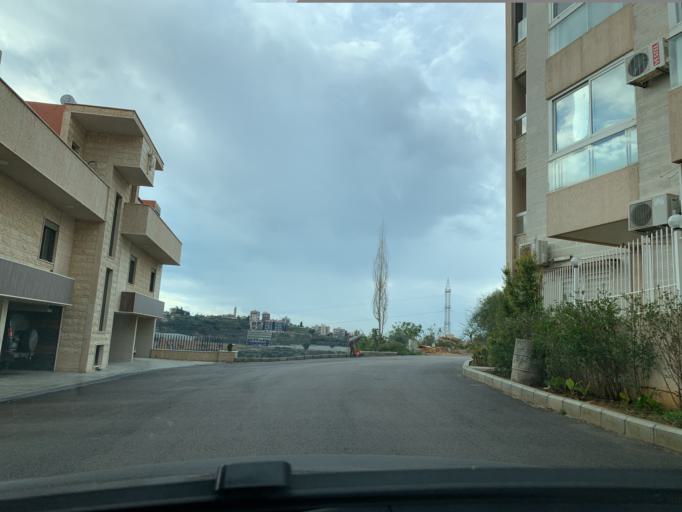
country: LB
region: Mont-Liban
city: Baabda
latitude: 33.8490
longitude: 35.5661
